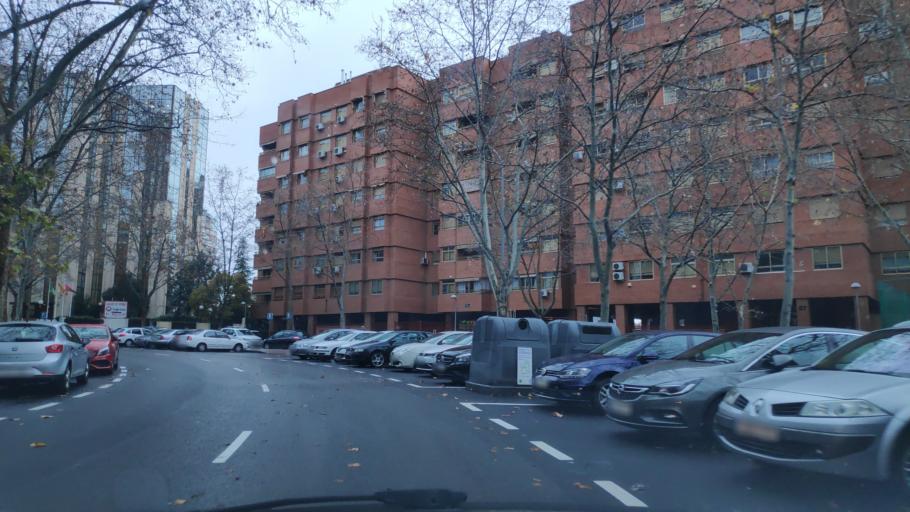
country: ES
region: Madrid
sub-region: Provincia de Madrid
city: Pinar de Chamartin
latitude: 40.4826
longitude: -3.6674
